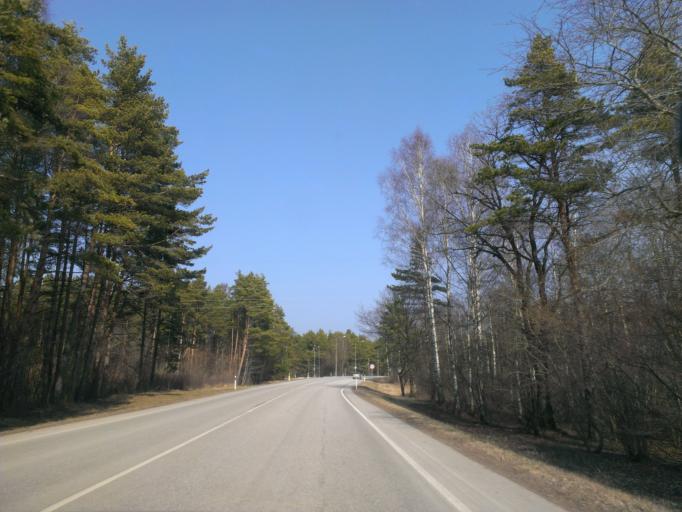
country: EE
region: Saare
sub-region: Orissaare vald
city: Orissaare
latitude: 58.5549
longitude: 23.0653
